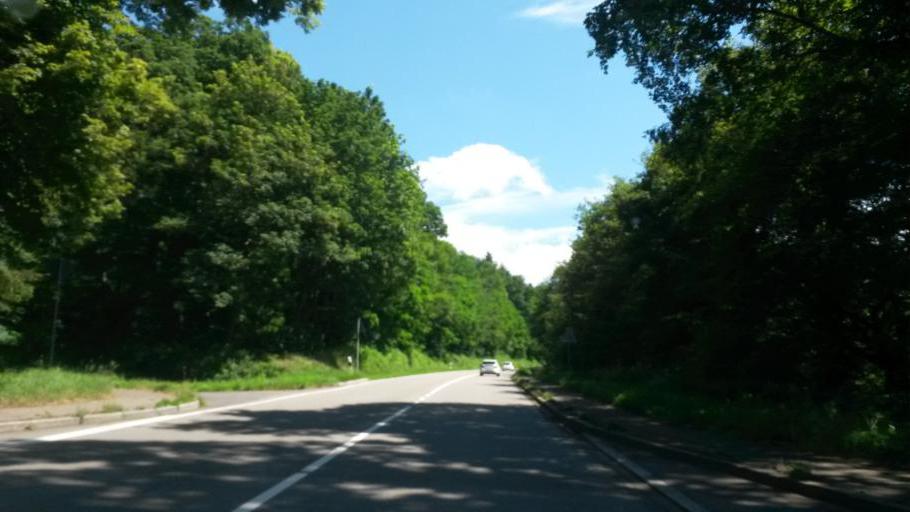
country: DE
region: Baden-Wuerttemberg
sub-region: Karlsruhe Region
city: Pforzheim
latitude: 48.8725
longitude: 8.6904
